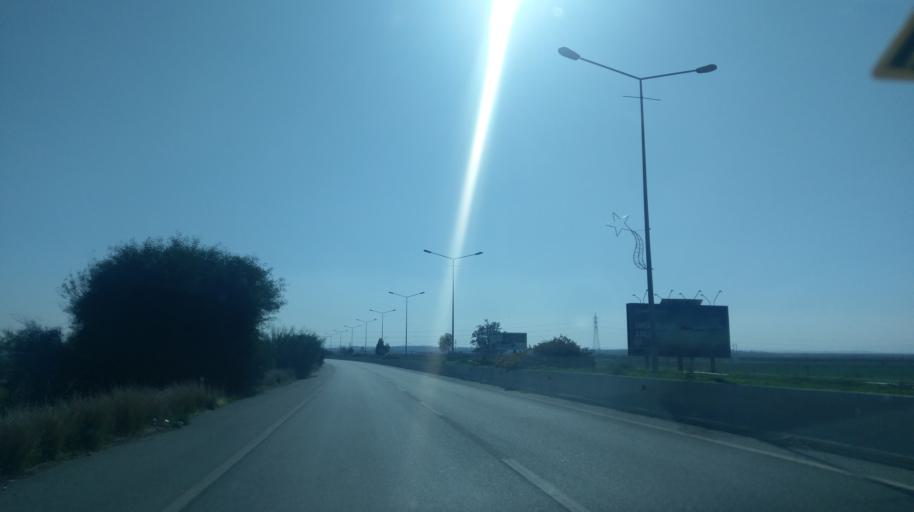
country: CY
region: Lefkosia
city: Geri
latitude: 35.1981
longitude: 33.5005
